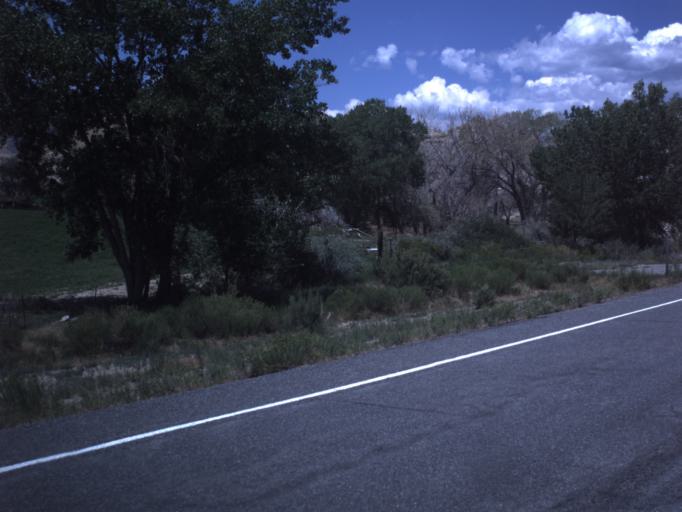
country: US
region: Utah
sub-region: Emery County
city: Orangeville
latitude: 39.2294
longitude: -111.0741
